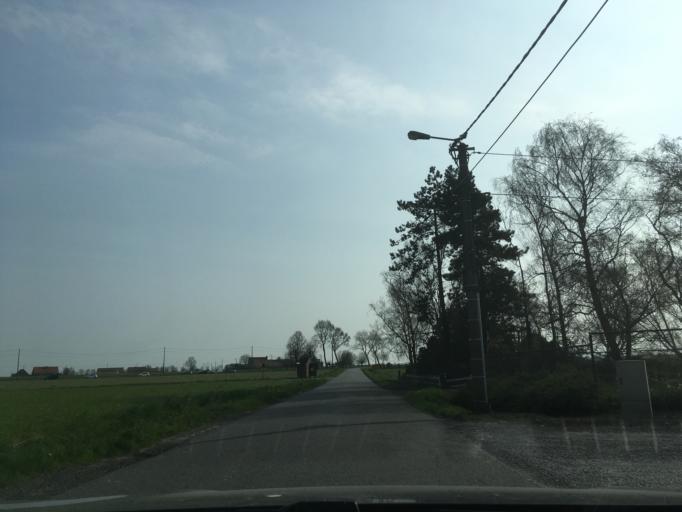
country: BE
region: Flanders
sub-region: Provincie West-Vlaanderen
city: Lichtervelde
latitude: 51.0168
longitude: 3.1830
